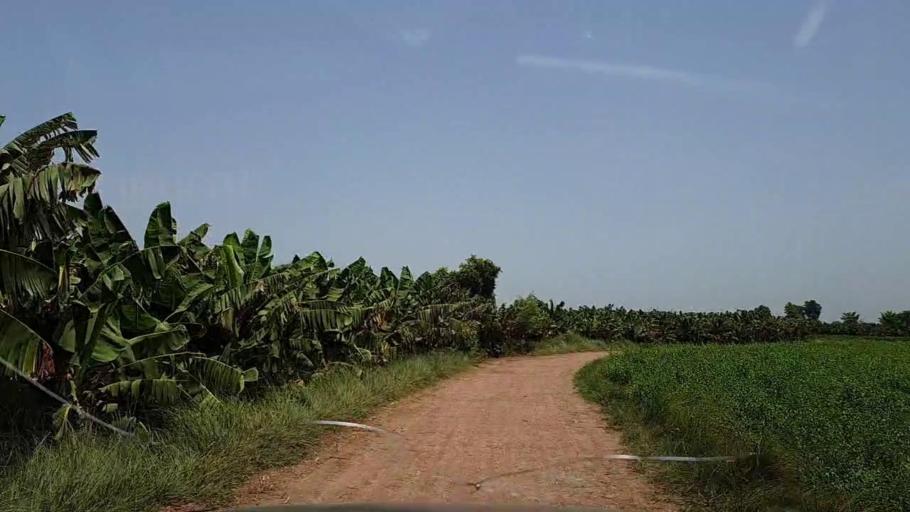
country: PK
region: Sindh
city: Tharu Shah
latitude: 26.9341
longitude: 68.0367
